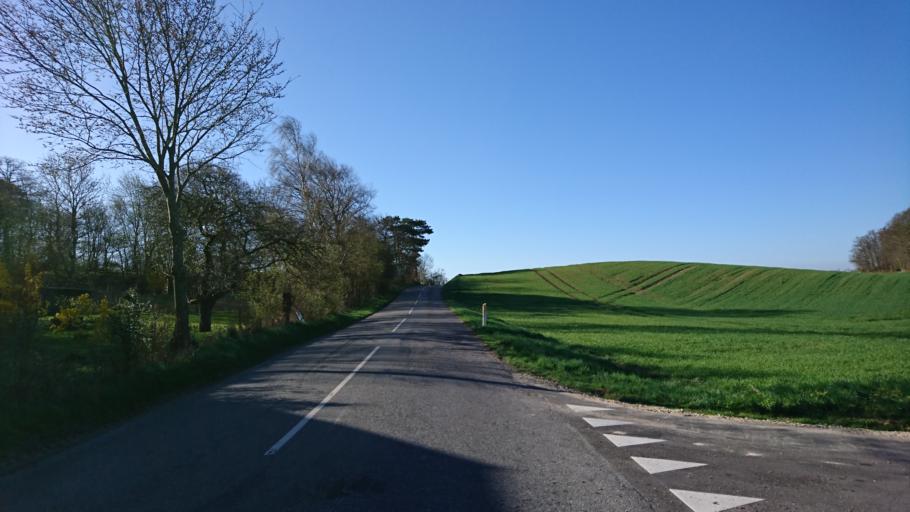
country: DK
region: Capital Region
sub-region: Frederikssund Kommune
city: Skibby
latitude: 55.7374
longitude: 11.9286
